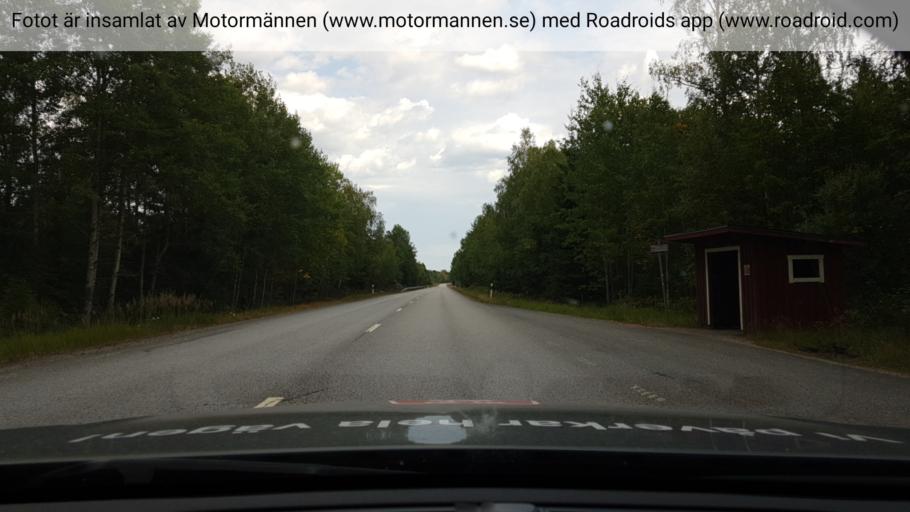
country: SE
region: Uppsala
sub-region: Heby Kommun
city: Morgongava
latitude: 59.8929
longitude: 17.1532
